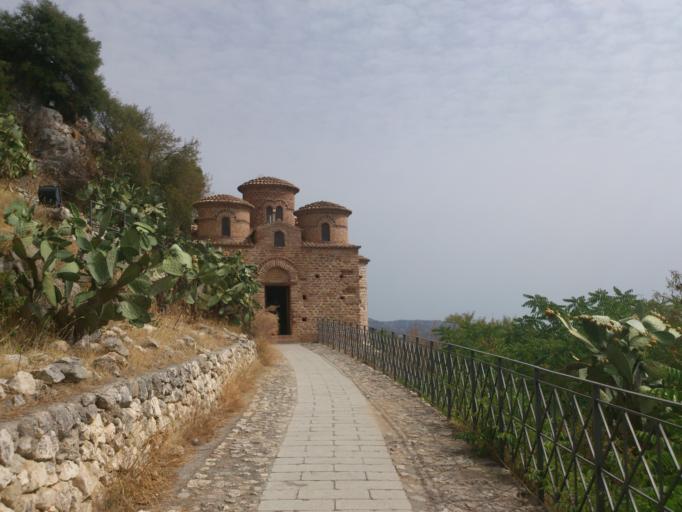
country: IT
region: Calabria
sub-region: Provincia di Reggio Calabria
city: Stilo
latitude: 38.4799
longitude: 16.4680
